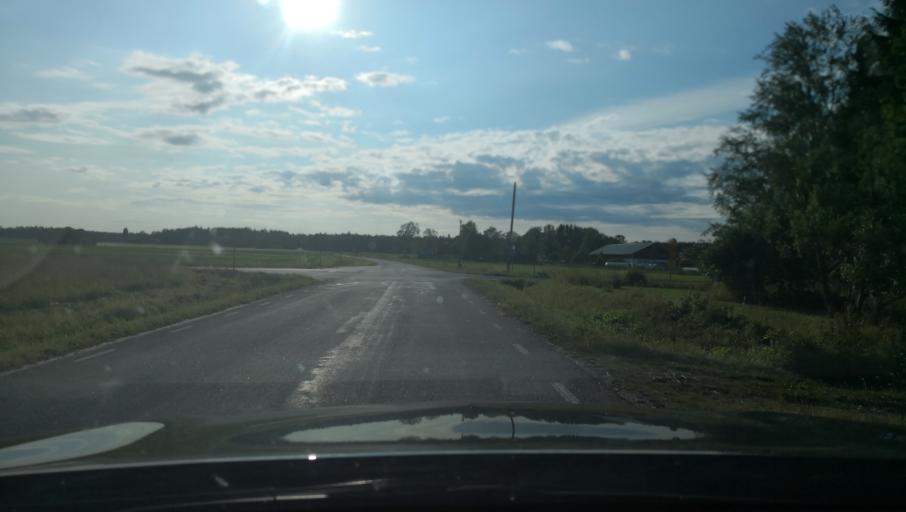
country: SE
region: Uppsala
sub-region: Osthammars Kommun
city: Osterbybruk
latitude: 60.0185
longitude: 17.9762
